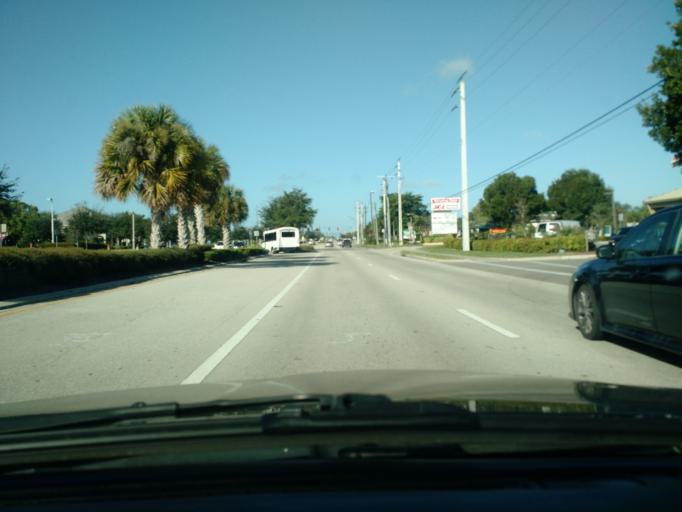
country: US
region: Florida
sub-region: Lee County
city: Bonita Springs
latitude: 26.3308
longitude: -81.8005
